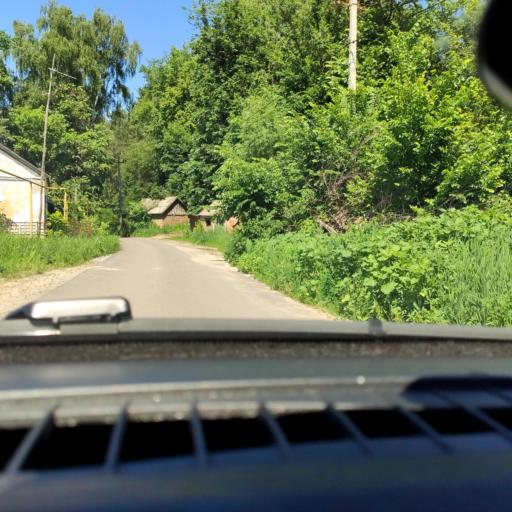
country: RU
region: Voronezj
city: Podgornoye
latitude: 51.7886
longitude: 39.1343
